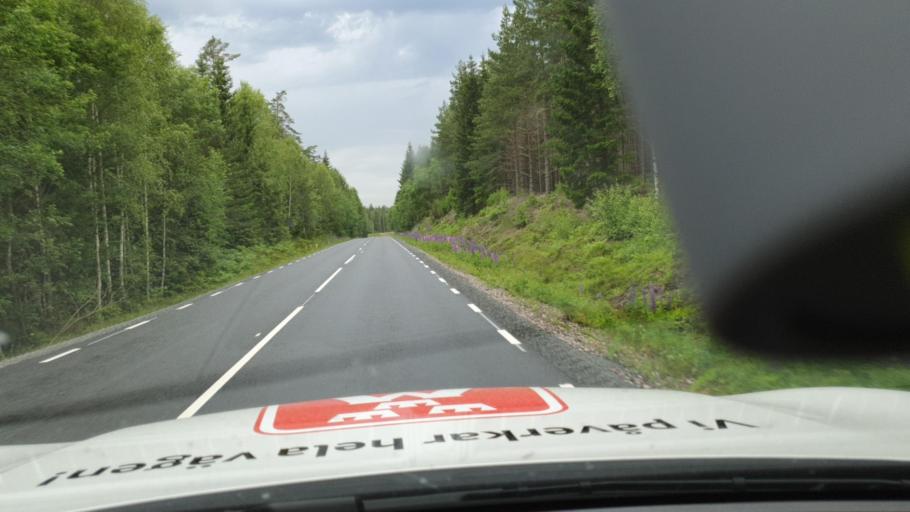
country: SE
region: OErebro
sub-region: Laxa Kommun
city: Laxa
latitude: 58.9037
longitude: 14.4682
